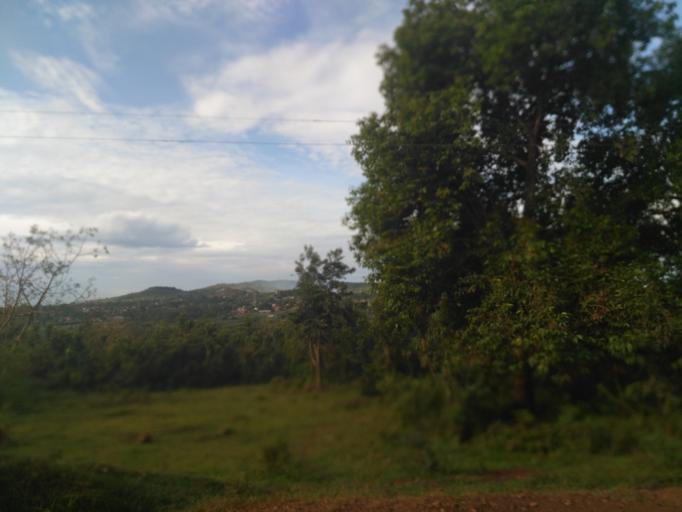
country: UG
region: Eastern Region
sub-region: Jinja District
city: Jinja
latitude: 0.4662
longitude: 33.1756
